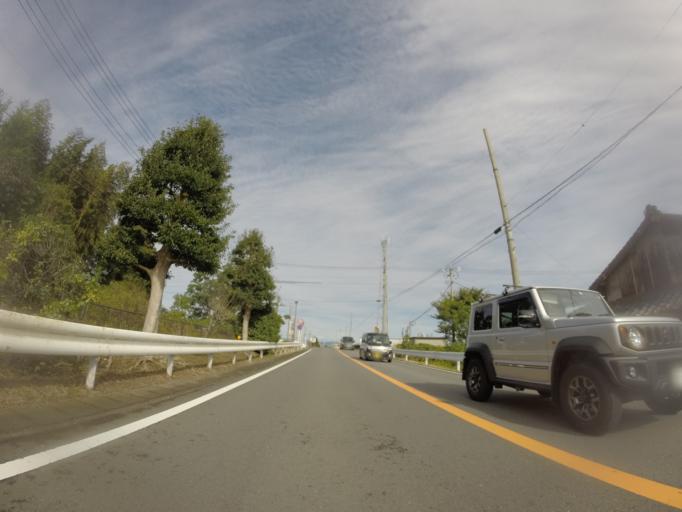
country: JP
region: Shizuoka
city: Shimada
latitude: 34.7799
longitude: 138.2486
